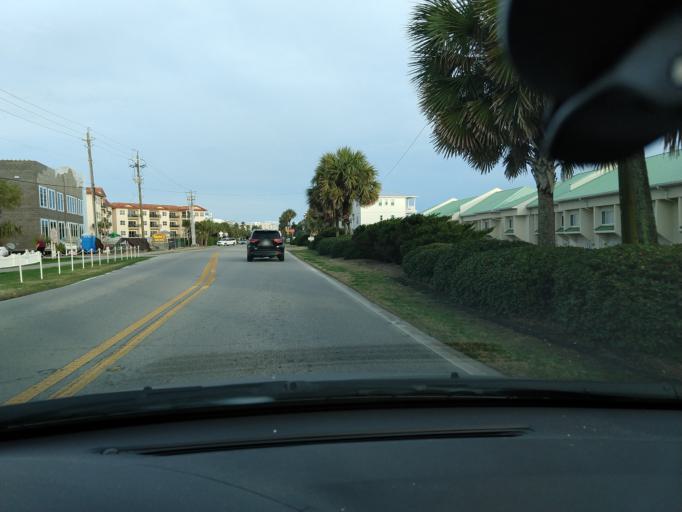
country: US
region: Florida
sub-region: Walton County
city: Miramar Beach
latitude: 30.3777
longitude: -86.3818
